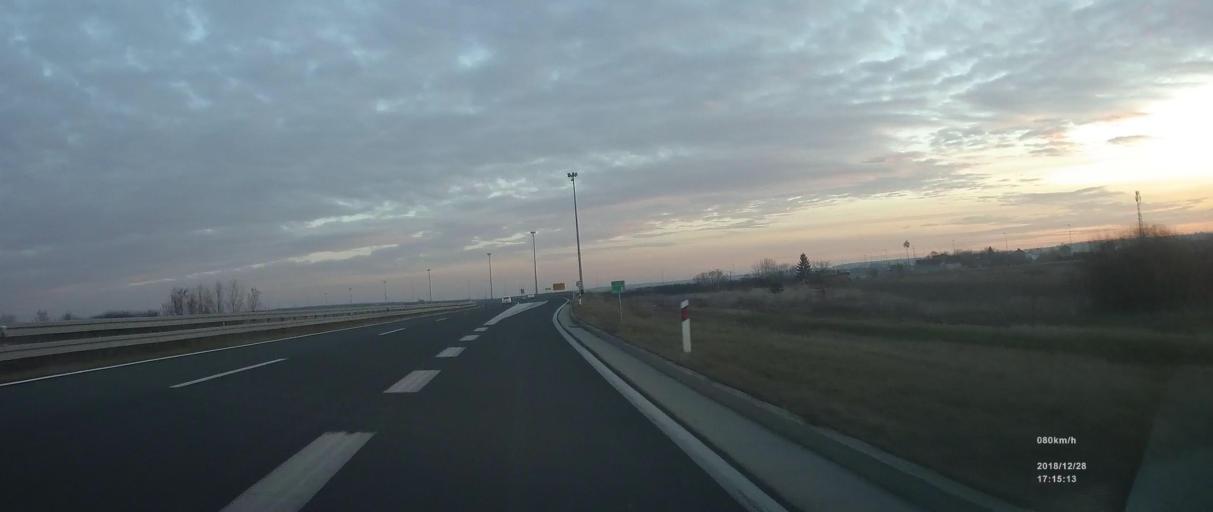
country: HR
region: Zagrebacka
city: Gradici
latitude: 45.6959
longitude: 16.0617
